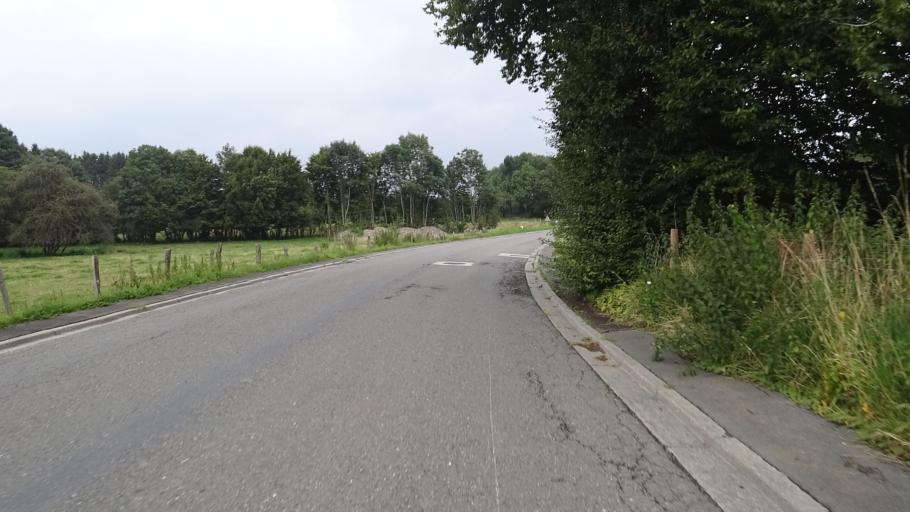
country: BE
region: Wallonia
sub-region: Province du Luxembourg
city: Chiny
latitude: 49.8089
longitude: 5.3279
